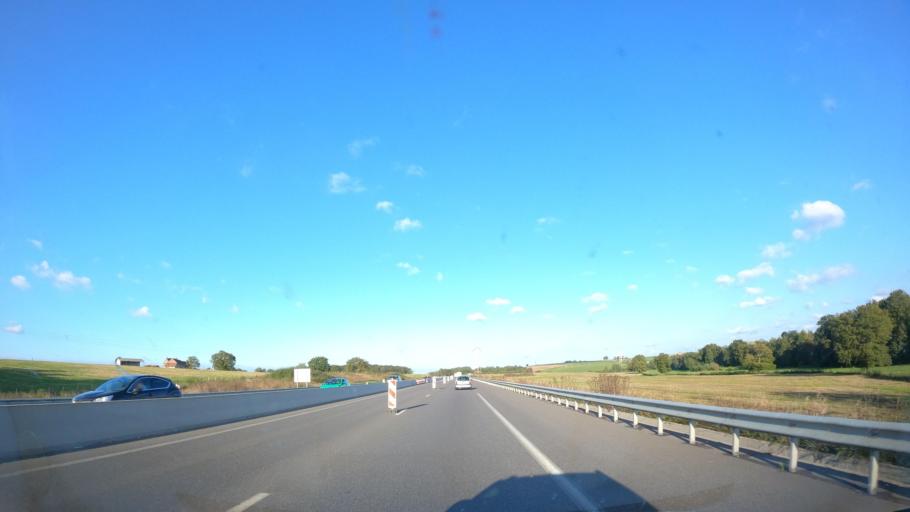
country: FR
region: Bourgogne
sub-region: Departement de Saone-et-Loire
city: Saint-Eusebe
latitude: 46.7117
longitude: 4.4301
